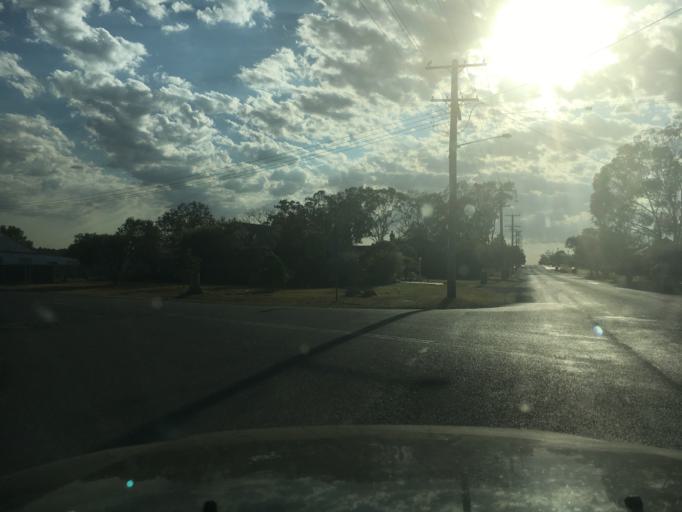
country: AU
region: New South Wales
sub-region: Cessnock
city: Branxton
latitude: -32.6561
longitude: 151.3638
